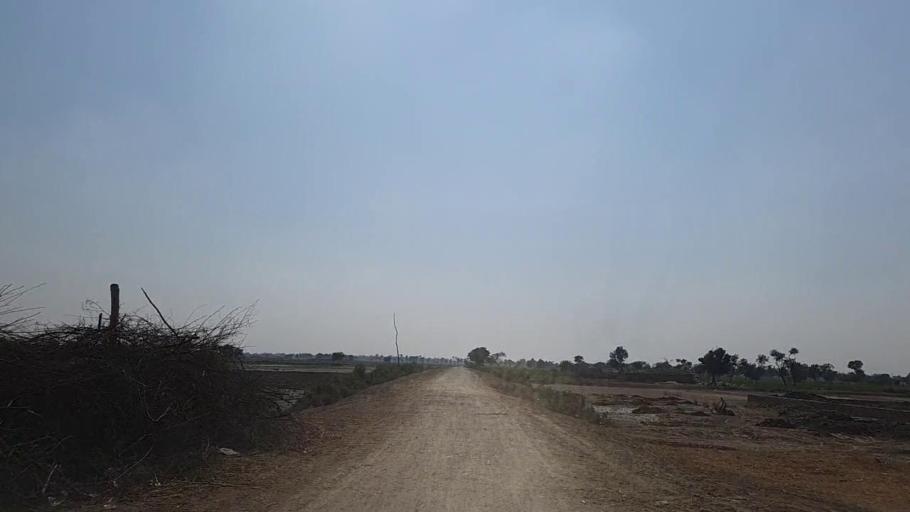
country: PK
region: Sindh
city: Daur
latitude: 26.4563
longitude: 68.2708
